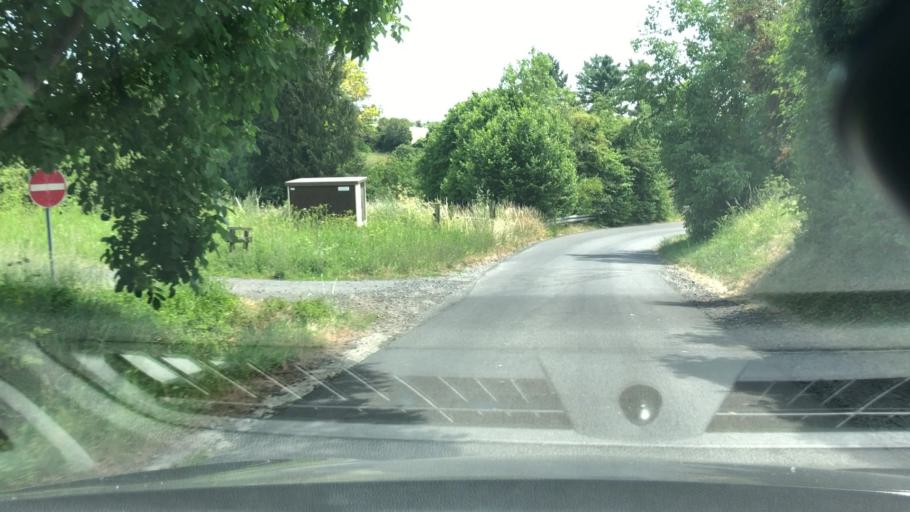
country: DE
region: Hesse
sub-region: Regierungsbezirk Darmstadt
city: Langenselbold
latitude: 50.2369
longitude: 9.0569
